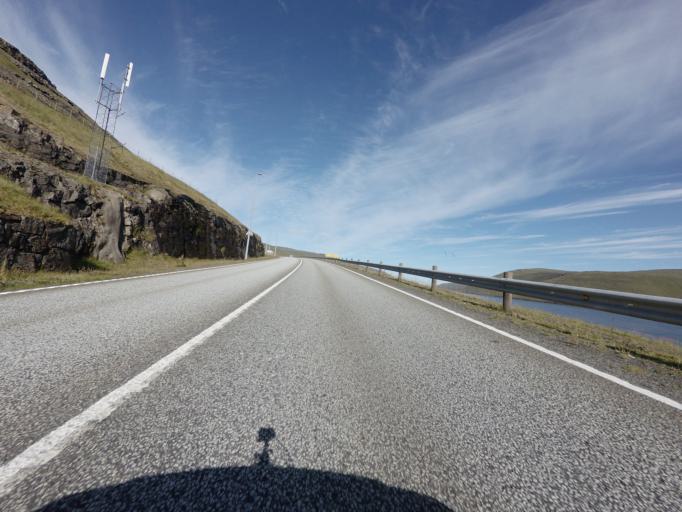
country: FO
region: Streymoy
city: Vestmanna
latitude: 62.0994
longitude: -7.1179
